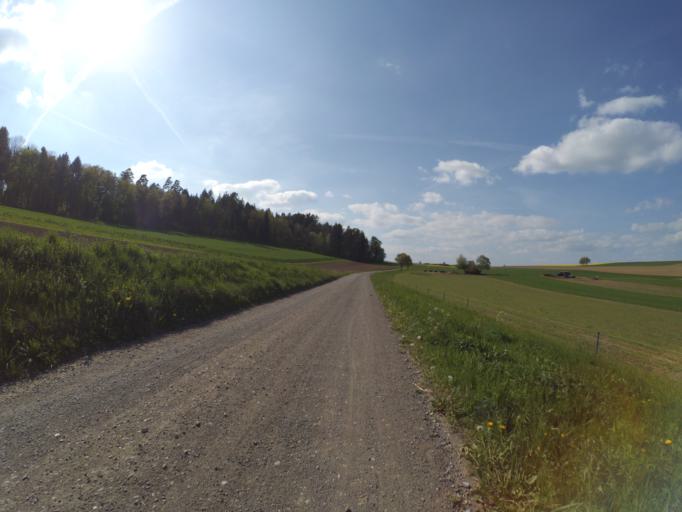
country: CH
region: Thurgau
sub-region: Frauenfeld District
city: Diessenhofen
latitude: 47.6559
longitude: 8.7602
